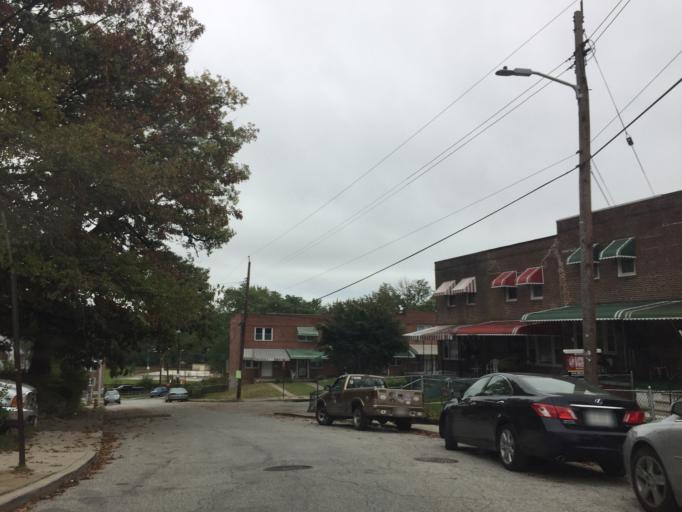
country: US
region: Maryland
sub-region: City of Baltimore
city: Baltimore
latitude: 39.3442
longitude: -76.6066
